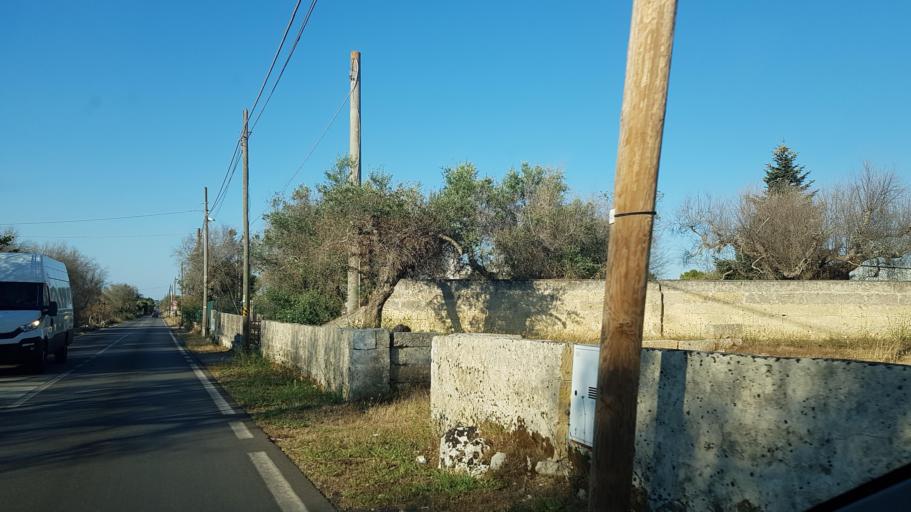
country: IT
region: Apulia
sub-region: Provincia di Lecce
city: Andrano
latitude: 39.9909
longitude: 18.3854
